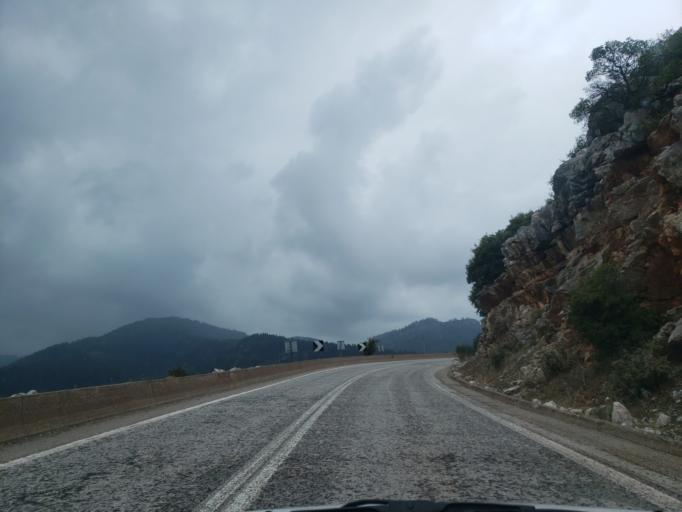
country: GR
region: Central Greece
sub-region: Nomos Fokidos
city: Amfissa
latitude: 38.6377
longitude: 22.3858
